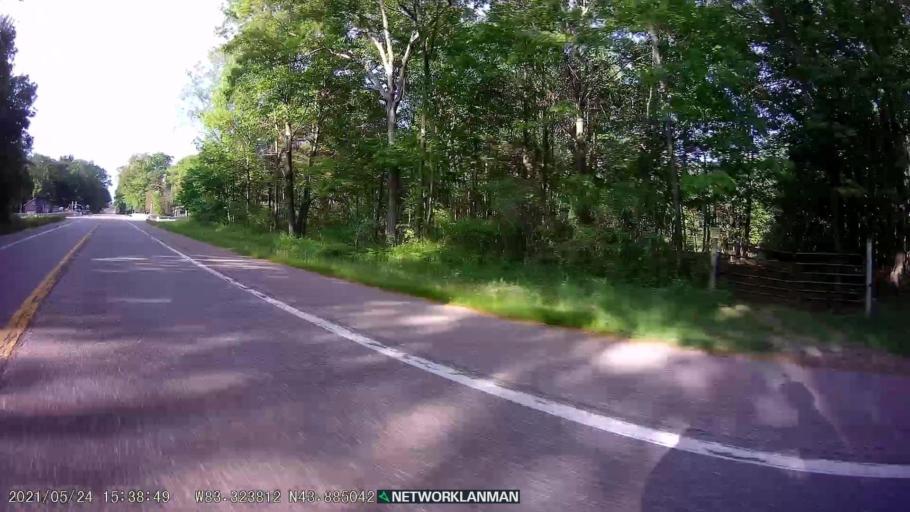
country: US
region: Michigan
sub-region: Huron County
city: Pigeon
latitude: 43.8854
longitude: -83.3238
